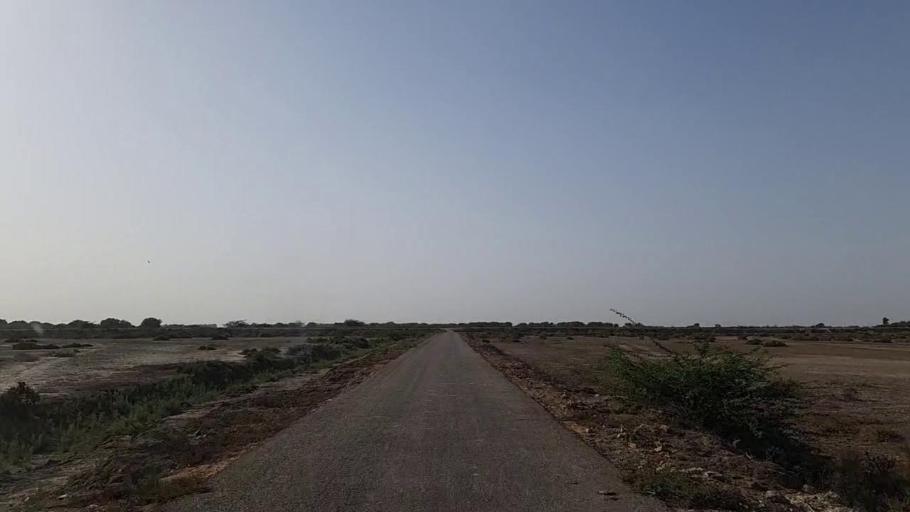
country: PK
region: Sindh
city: Jati
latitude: 24.3033
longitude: 68.1968
